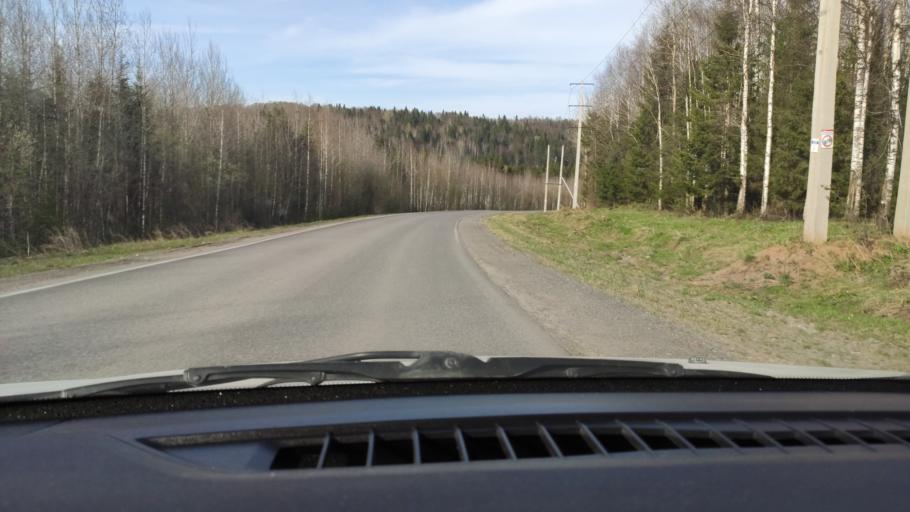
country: RU
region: Perm
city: Novyye Lyady
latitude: 57.9582
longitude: 56.5359
